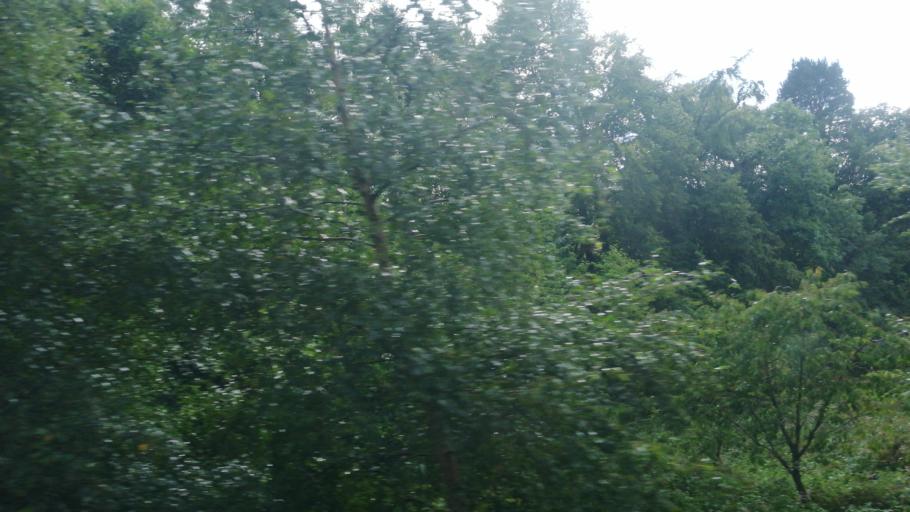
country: GB
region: Scotland
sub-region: Aberdeenshire
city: Insch
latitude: 57.3370
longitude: -2.6403
